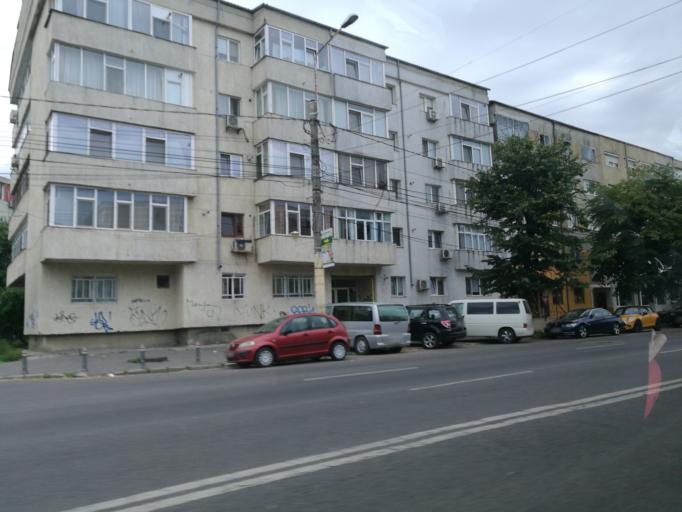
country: RO
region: Constanta
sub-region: Municipiul Constanta
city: Constanta
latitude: 44.1945
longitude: 28.6324
